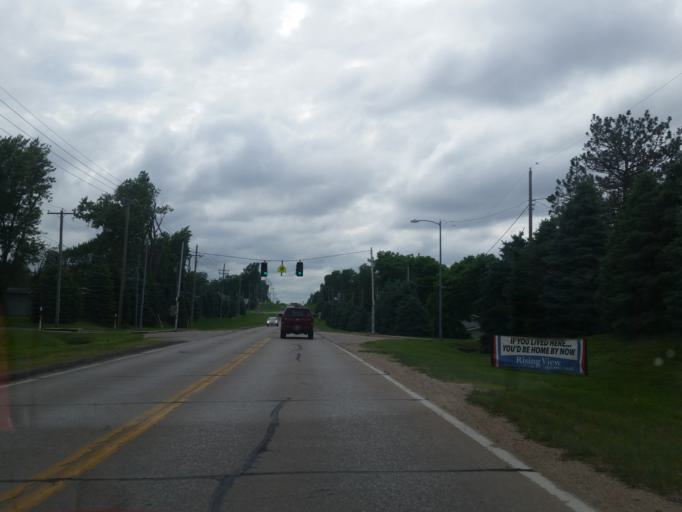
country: US
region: Nebraska
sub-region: Sarpy County
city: Offutt Air Force Base
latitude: 41.1218
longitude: -95.9579
